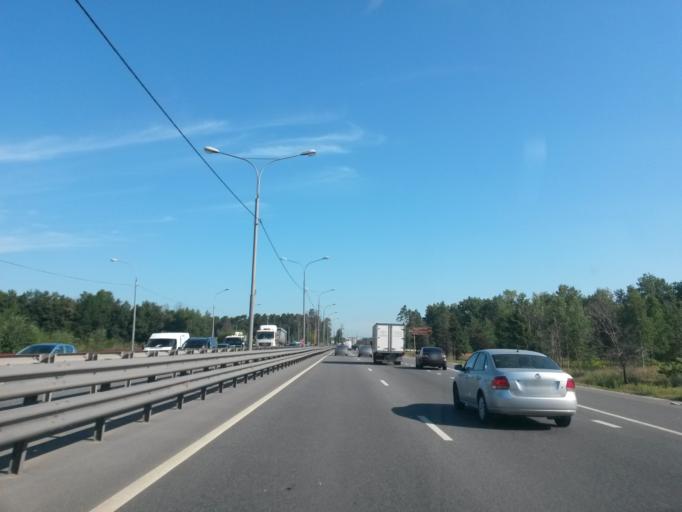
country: RU
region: Moskovskaya
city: Pushkino
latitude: 56.0069
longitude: 37.8778
